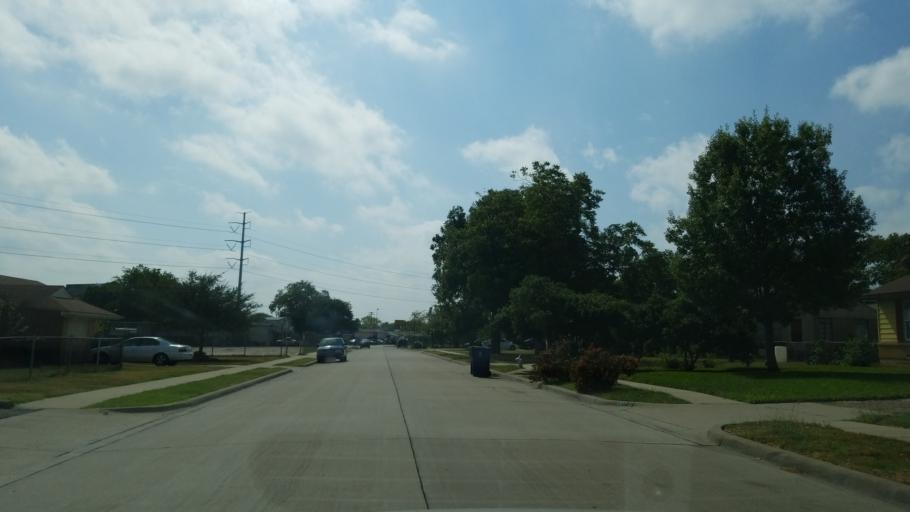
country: US
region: Texas
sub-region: Dallas County
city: Garland
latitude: 32.8938
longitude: -96.6516
